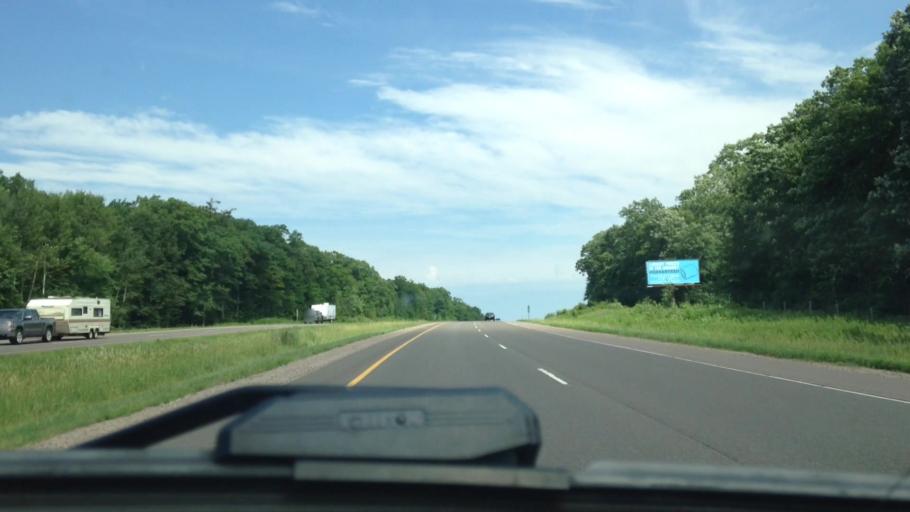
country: US
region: Wisconsin
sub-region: Washburn County
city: Spooner
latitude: 45.8316
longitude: -91.8582
